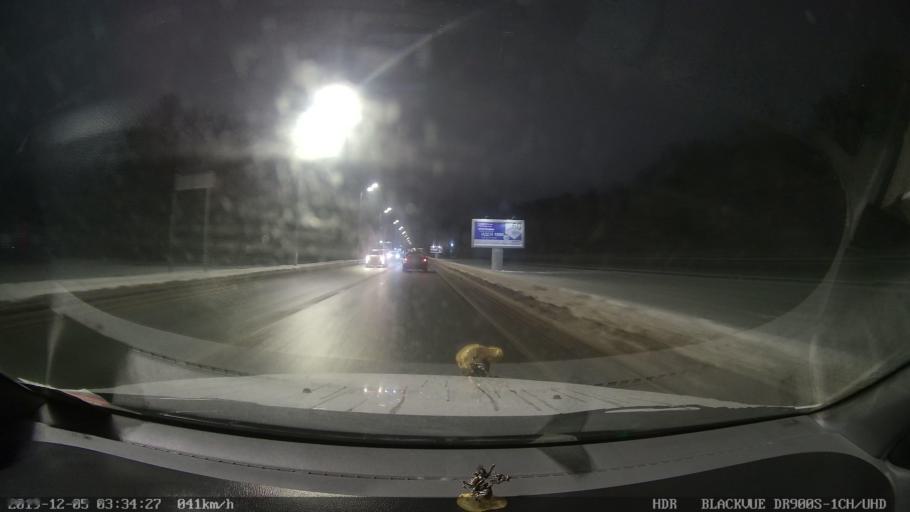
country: RU
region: Tatarstan
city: Stolbishchi
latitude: 55.6128
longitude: 49.2868
